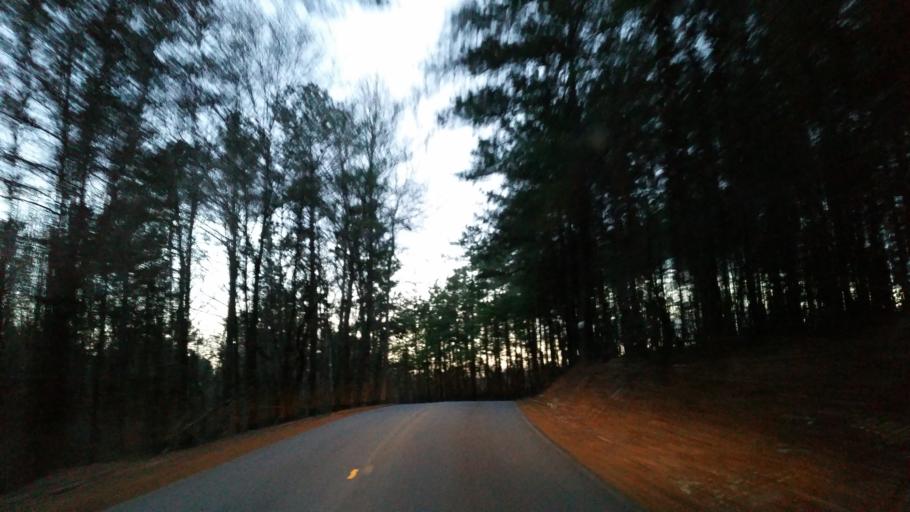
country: US
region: Georgia
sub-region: Cherokee County
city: Ball Ground
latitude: 34.3267
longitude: -84.3823
